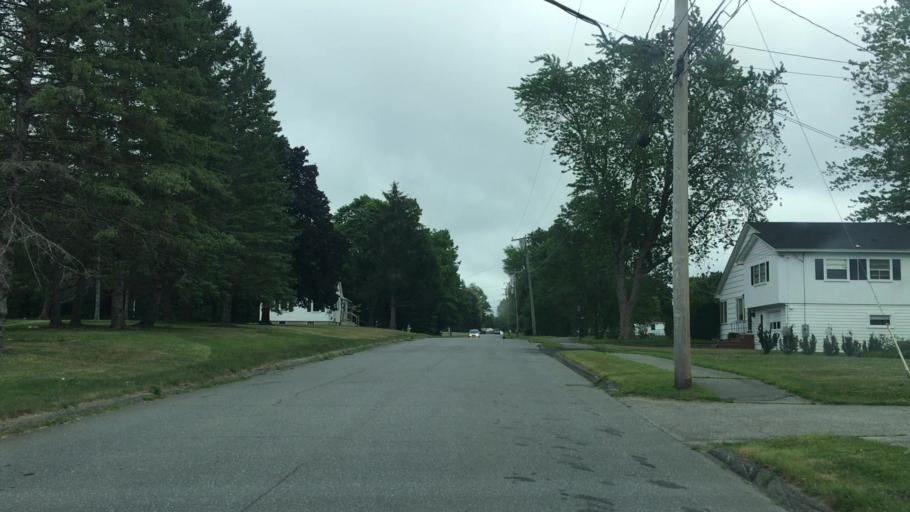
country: US
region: Maine
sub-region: Penobscot County
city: Brewer
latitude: 44.7883
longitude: -68.7520
